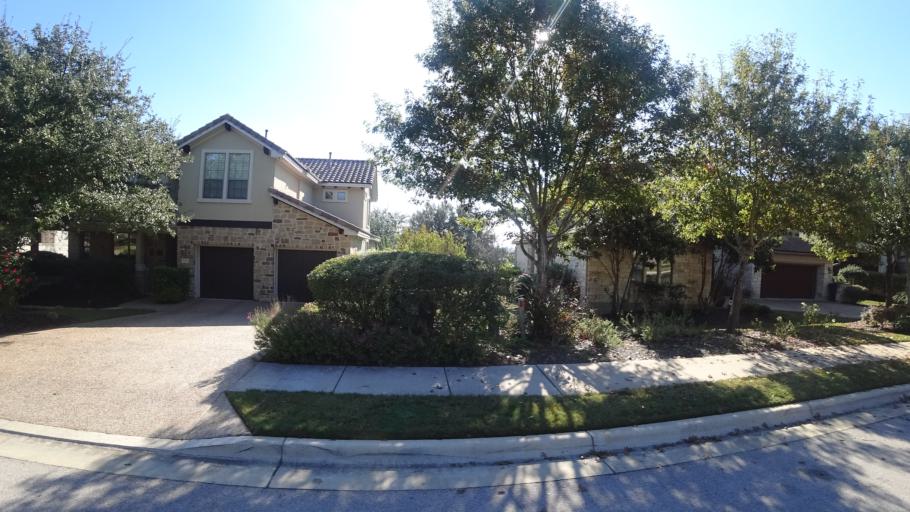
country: US
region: Texas
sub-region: Travis County
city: Bee Cave
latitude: 30.3523
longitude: -97.8932
